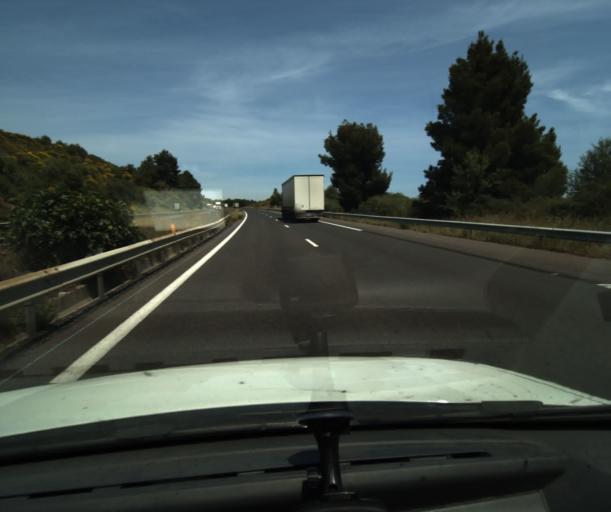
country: FR
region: Languedoc-Roussillon
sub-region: Departement des Pyrenees-Orientales
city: Banyuls-dels-Aspres
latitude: 42.5460
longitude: 2.8487
